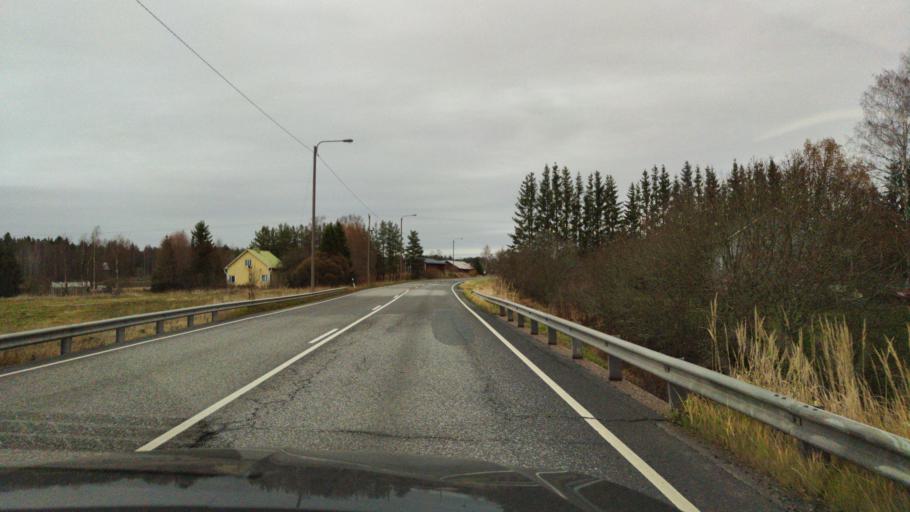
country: FI
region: Varsinais-Suomi
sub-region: Turku
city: Vahto
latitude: 60.6458
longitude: 22.4227
